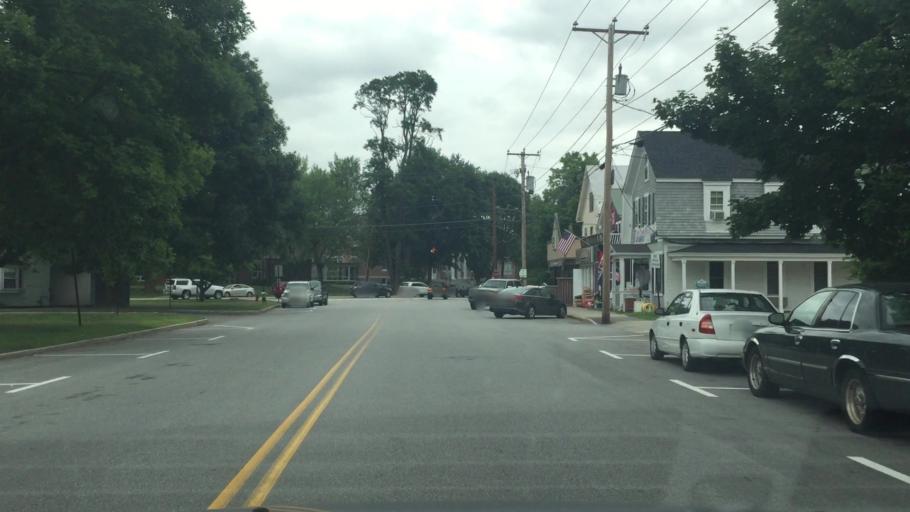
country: US
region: New Hampshire
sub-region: Carroll County
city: Conway
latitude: 43.9779
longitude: -71.1272
